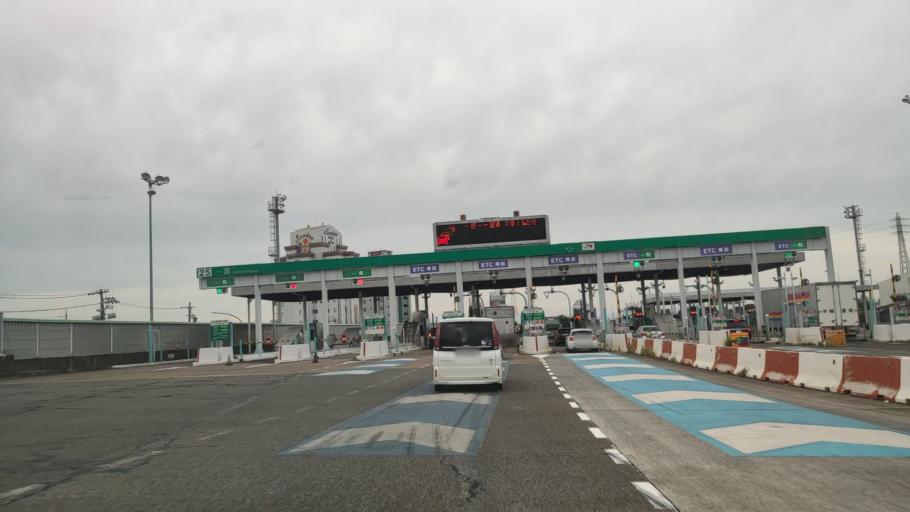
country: JP
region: Aichi
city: Iwakura
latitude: 35.2709
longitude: 136.8304
